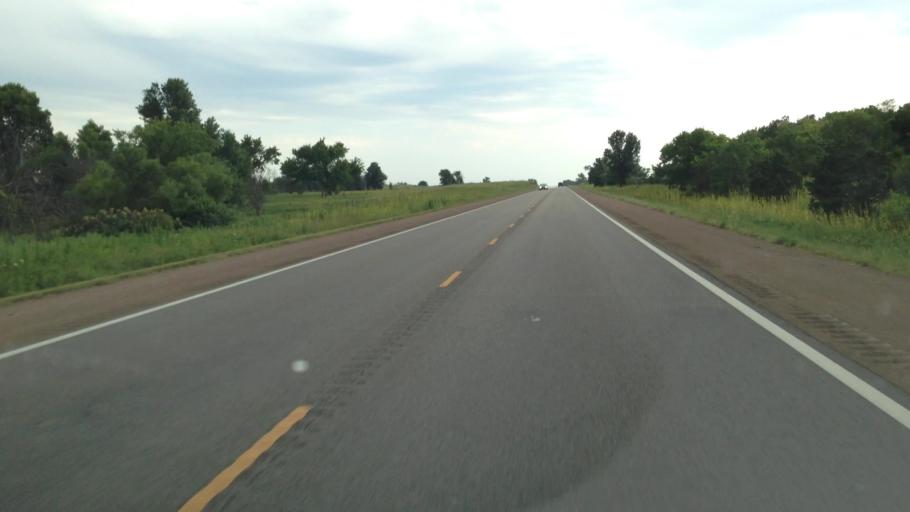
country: US
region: Kansas
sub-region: Woodson County
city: Yates Center
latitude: 38.0222
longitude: -95.7391
